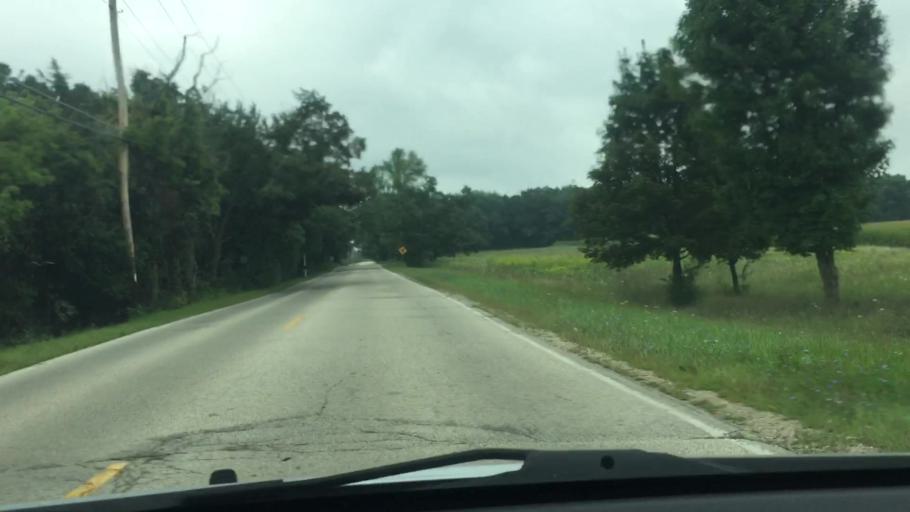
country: US
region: Wisconsin
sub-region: Waukesha County
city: Dousman
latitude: 43.0429
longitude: -88.4425
